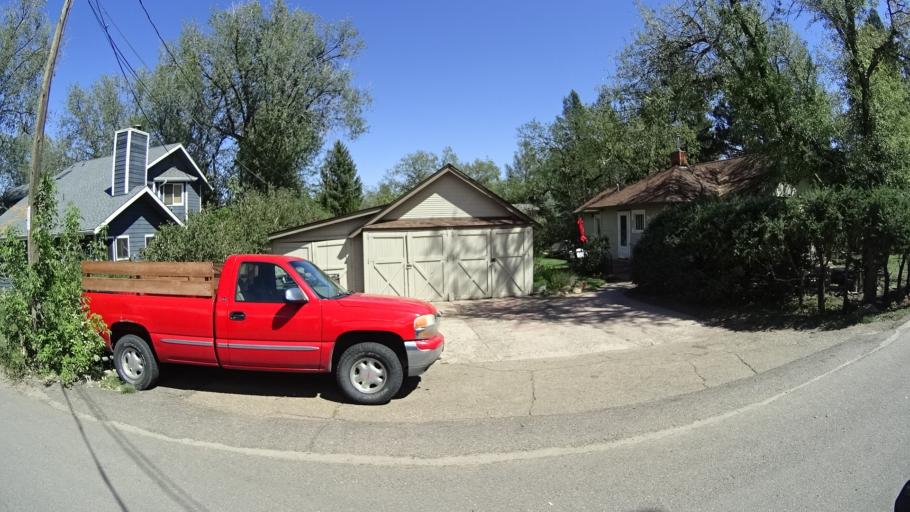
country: US
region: Colorado
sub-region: El Paso County
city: Colorado Springs
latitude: 38.8007
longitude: -104.8456
